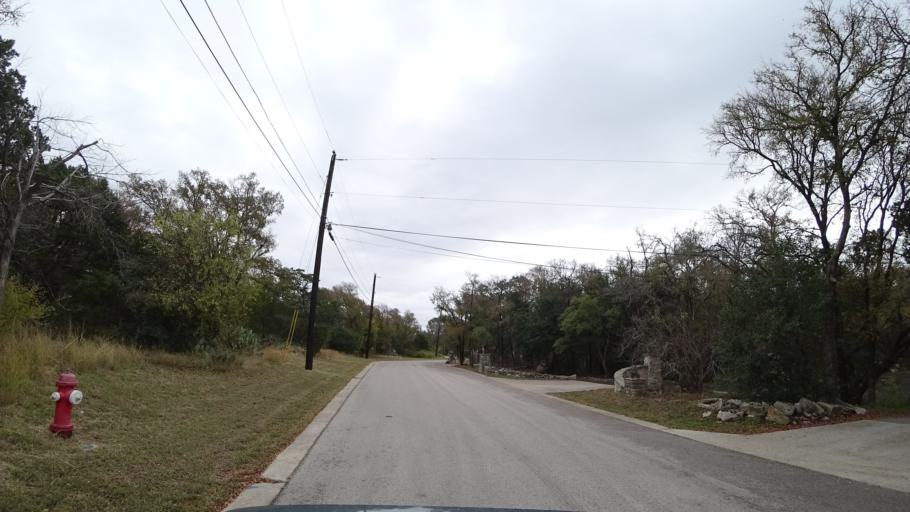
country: US
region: Texas
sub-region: Williamson County
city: Round Rock
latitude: 30.5145
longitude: -97.6986
